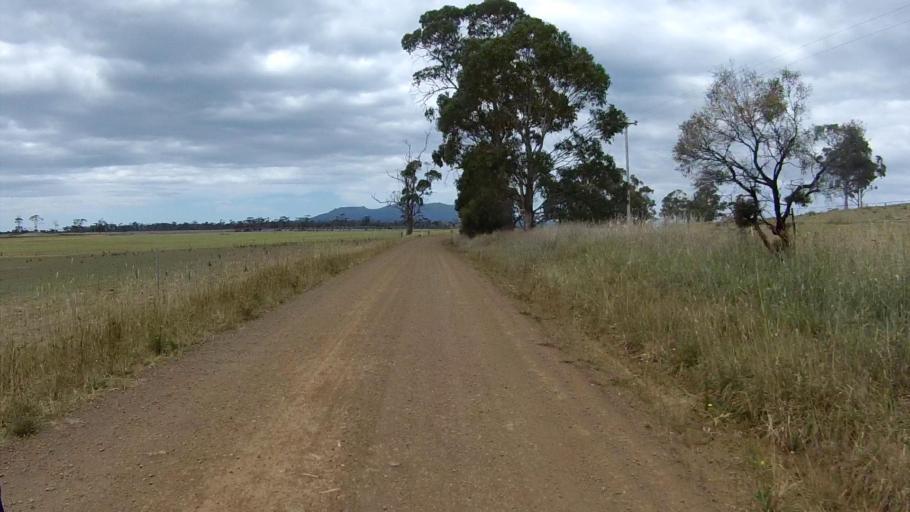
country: AU
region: Tasmania
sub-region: Sorell
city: Sorell
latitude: -42.6533
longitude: 147.9245
